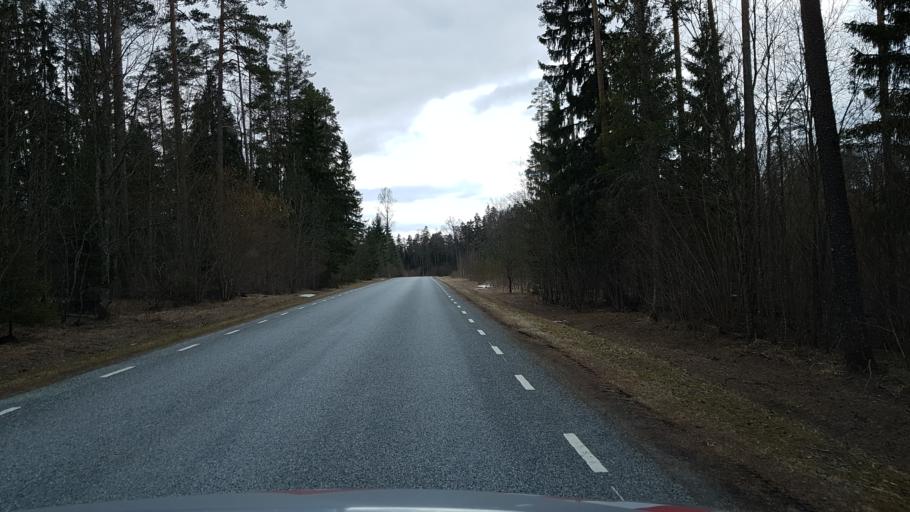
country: EE
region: Laeaene-Virumaa
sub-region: Tamsalu vald
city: Tamsalu
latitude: 59.2347
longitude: 26.1720
